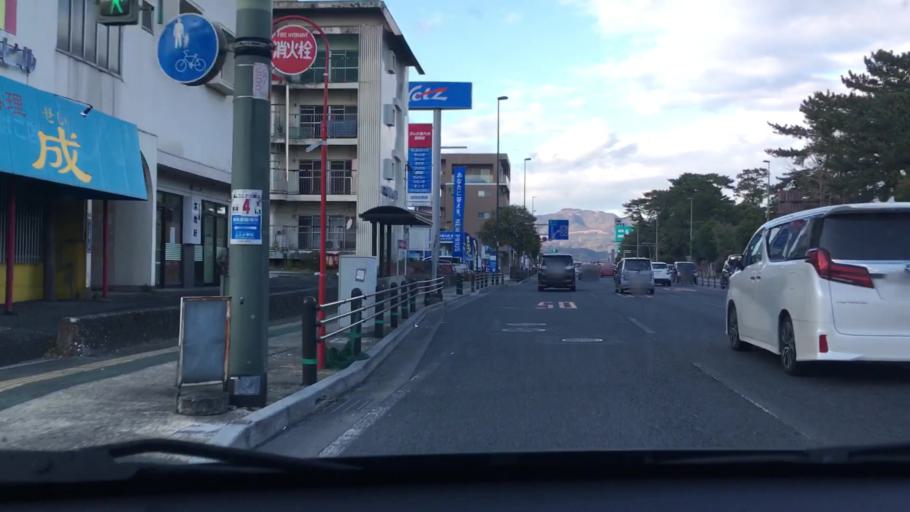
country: JP
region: Oita
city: Beppu
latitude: 33.3128
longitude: 131.5008
